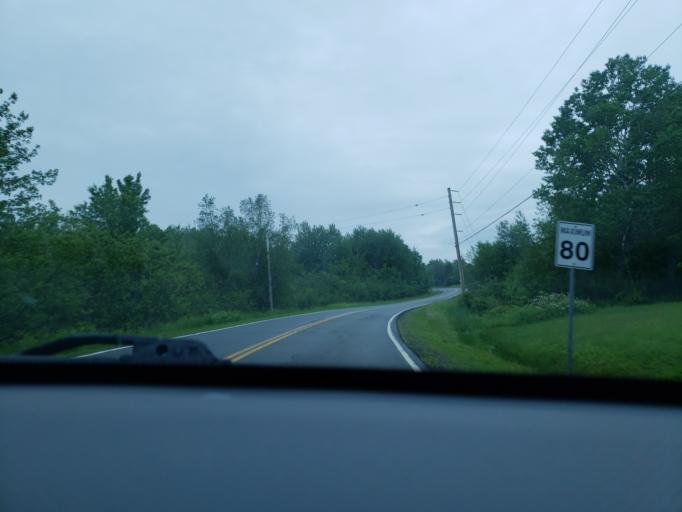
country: CA
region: Nova Scotia
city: Windsor
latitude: 45.0607
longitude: -63.9876
